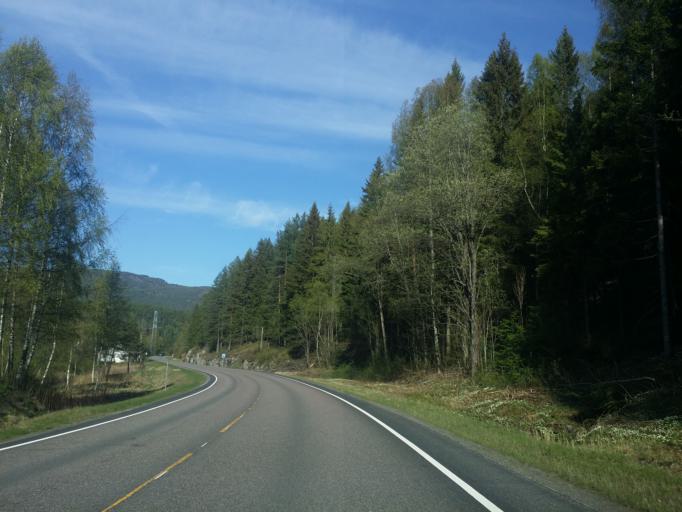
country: NO
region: Telemark
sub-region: Hjartdal
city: Sauland
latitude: 59.6089
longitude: 8.9754
